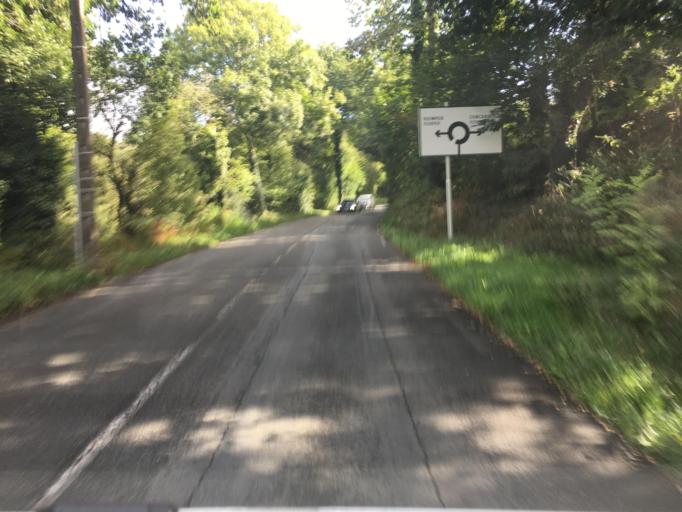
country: FR
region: Brittany
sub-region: Departement du Finistere
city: La Foret-Fouesnant
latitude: 47.9178
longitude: -3.9660
